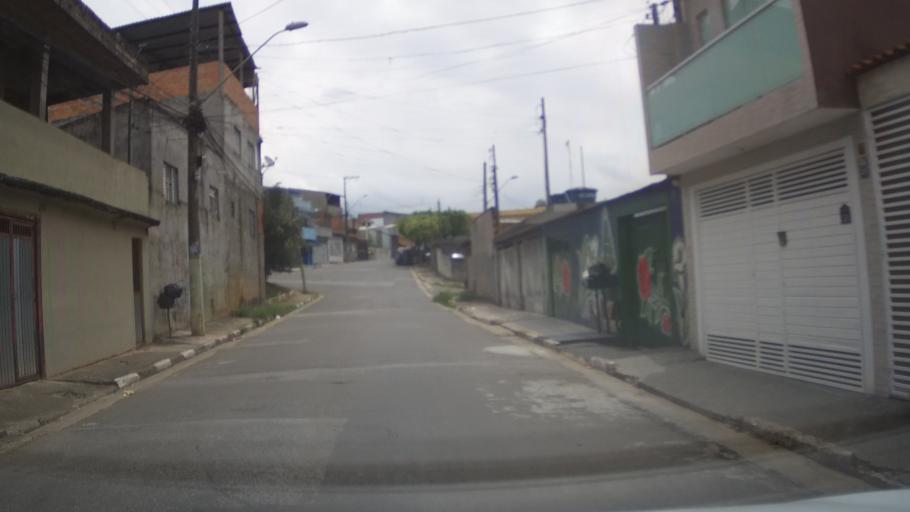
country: BR
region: Sao Paulo
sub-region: Itaquaquecetuba
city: Itaquaquecetuba
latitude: -23.4350
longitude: -46.4098
